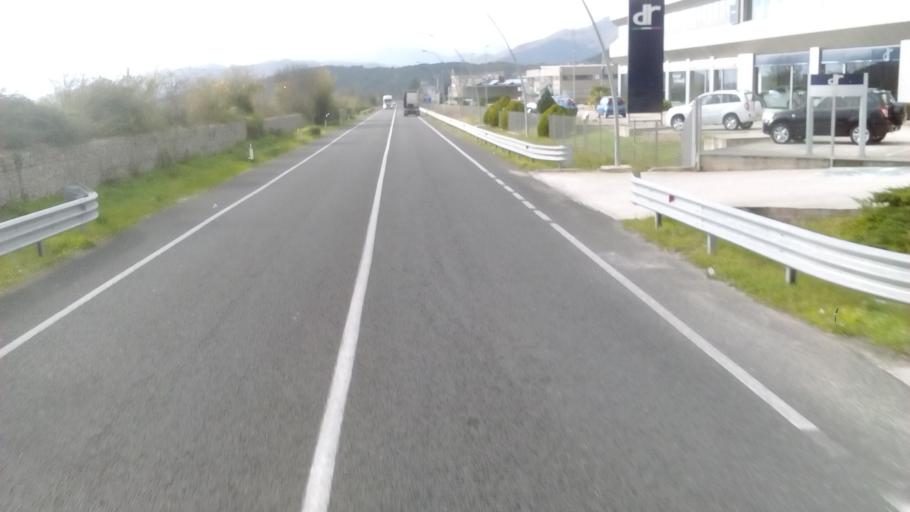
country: IT
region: Molise
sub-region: Provincia di Isernia
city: Macchia d'Isernia
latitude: 41.5635
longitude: 14.1903
